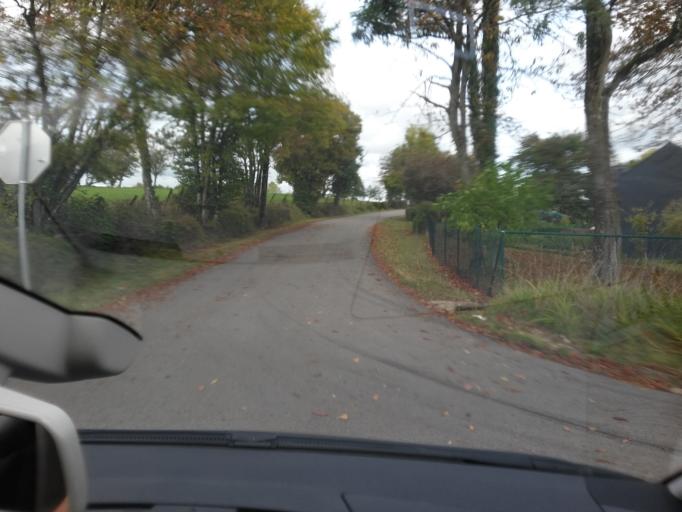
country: BE
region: Wallonia
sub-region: Province du Luxembourg
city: Arlon
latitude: 49.6613
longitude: 5.7643
